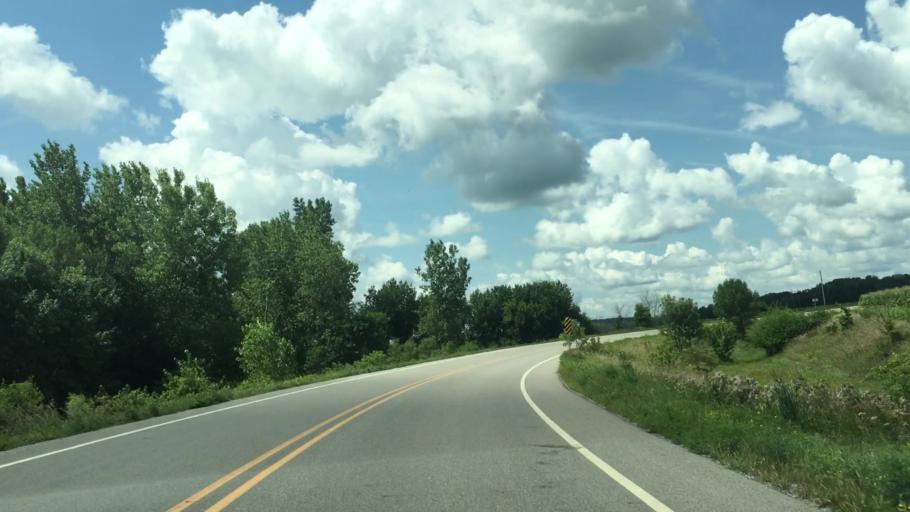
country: US
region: Iowa
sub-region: Linn County
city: Lisbon
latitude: 41.8416
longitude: -91.3968
